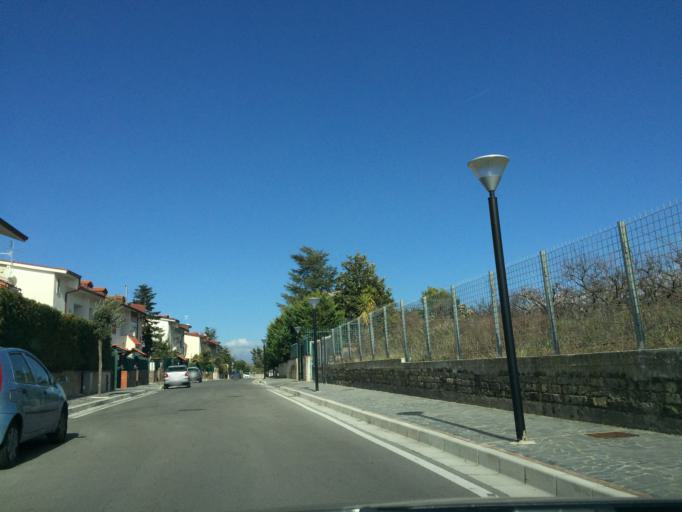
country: IT
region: Campania
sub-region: Provincia di Napoli
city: Pollena Trocchia
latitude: 40.8489
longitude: 14.3816
